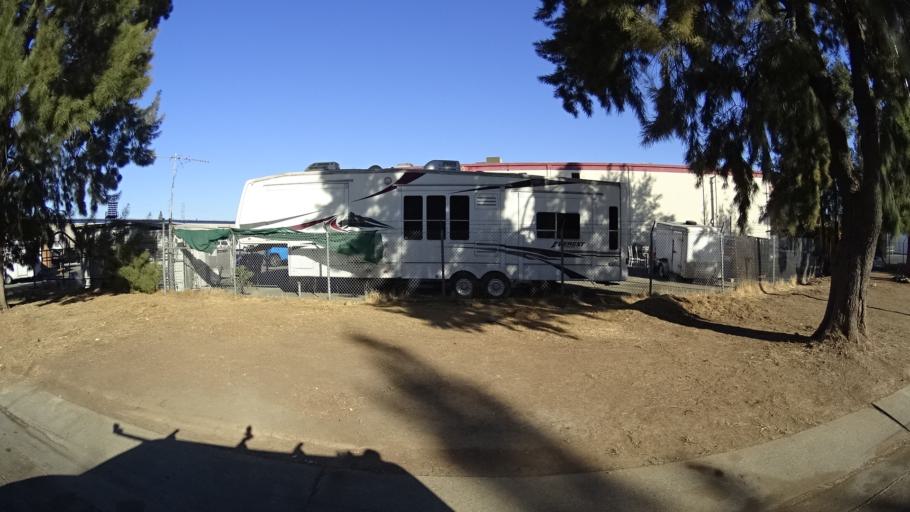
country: US
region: California
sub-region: Sacramento County
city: Florin
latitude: 38.5137
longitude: -121.4060
